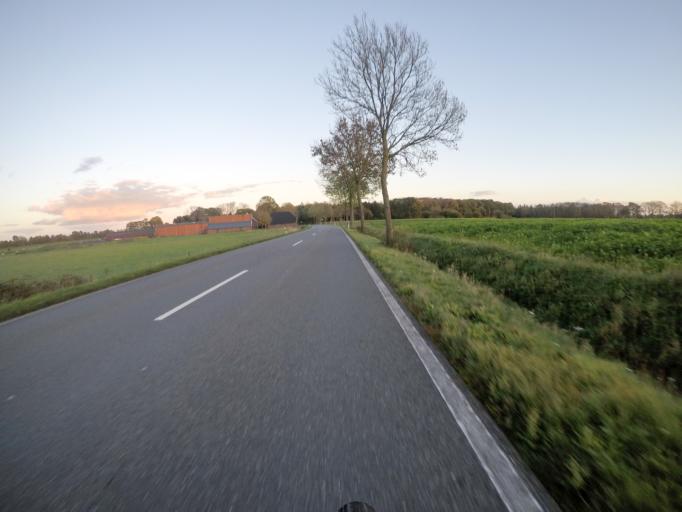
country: DE
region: North Rhine-Westphalia
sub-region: Regierungsbezirk Munster
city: Isselburg
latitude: 51.8438
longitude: 6.4855
